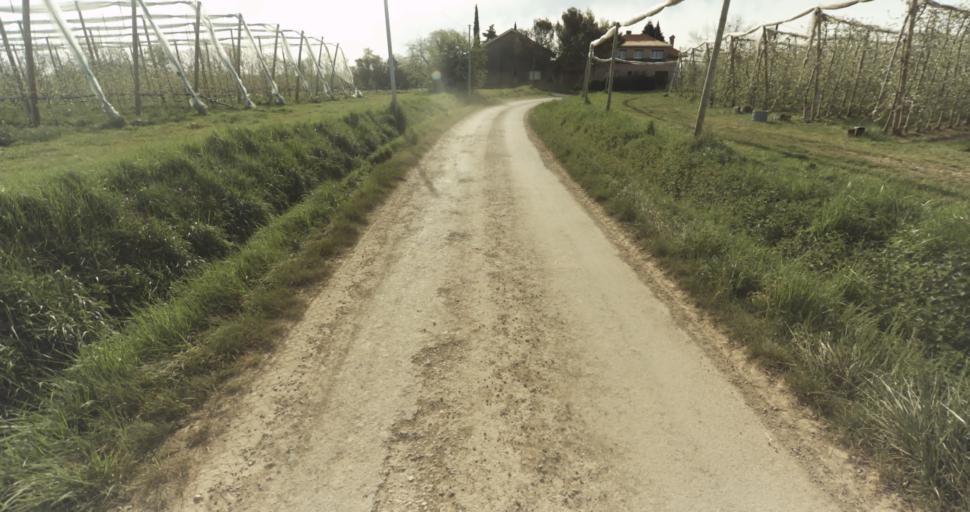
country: FR
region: Midi-Pyrenees
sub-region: Departement du Tarn-et-Garonne
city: Moissac
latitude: 44.1009
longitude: 1.1220
